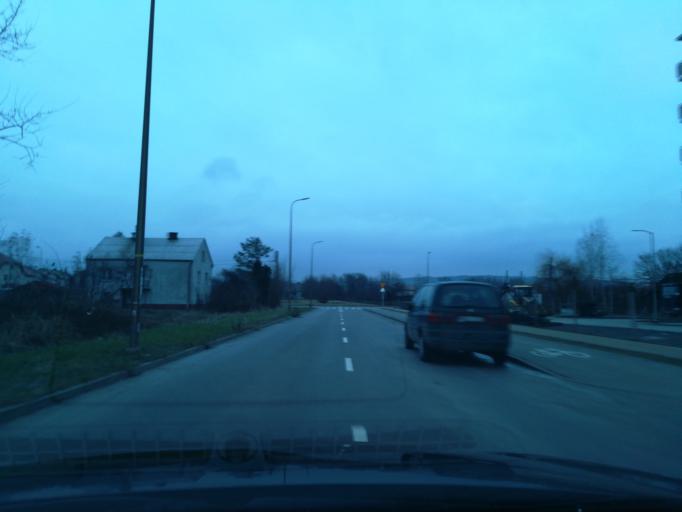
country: PL
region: Subcarpathian Voivodeship
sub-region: Rzeszow
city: Rzeszow
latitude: 50.0111
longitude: 22.0091
